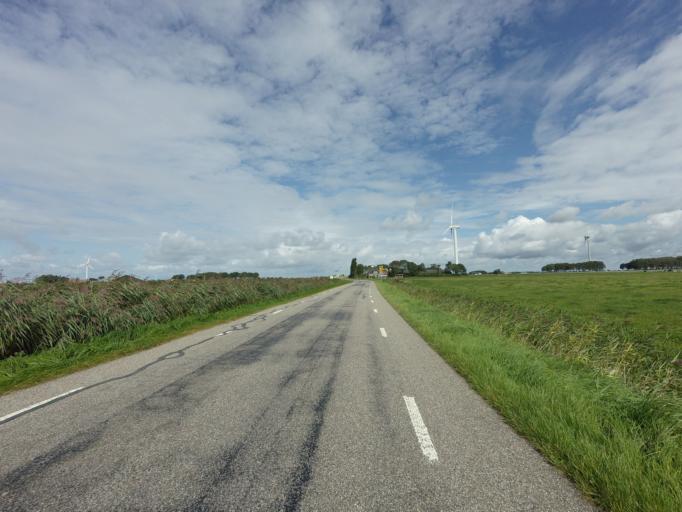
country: NL
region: Friesland
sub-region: Sudwest Fryslan
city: Makkum
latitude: 53.0885
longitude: 5.4211
